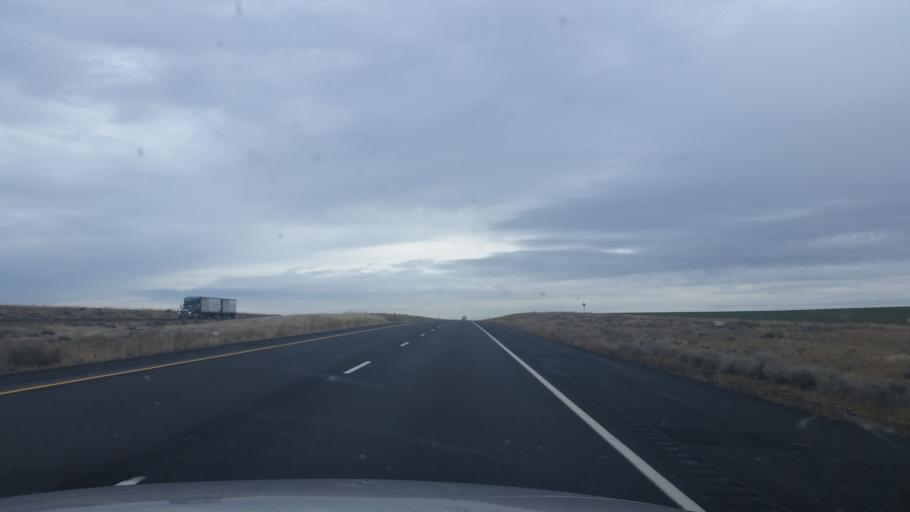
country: US
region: Washington
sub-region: Grant County
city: Warden
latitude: 47.0865
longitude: -118.7674
